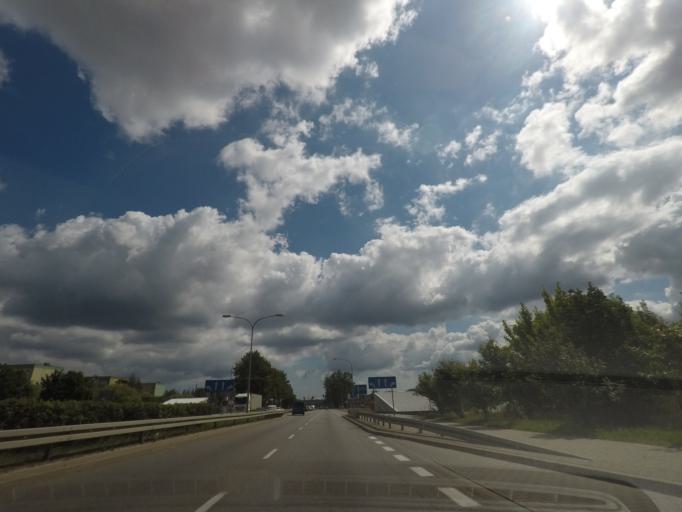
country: PL
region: Pomeranian Voivodeship
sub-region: Powiat wejherowski
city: Wejherowo
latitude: 54.6052
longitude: 18.2392
